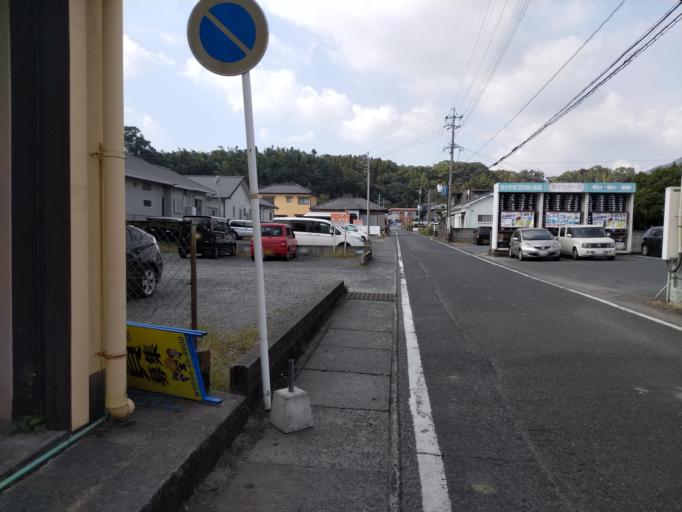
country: JP
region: Kagoshima
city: Kanoya
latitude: 31.3941
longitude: 130.8540
